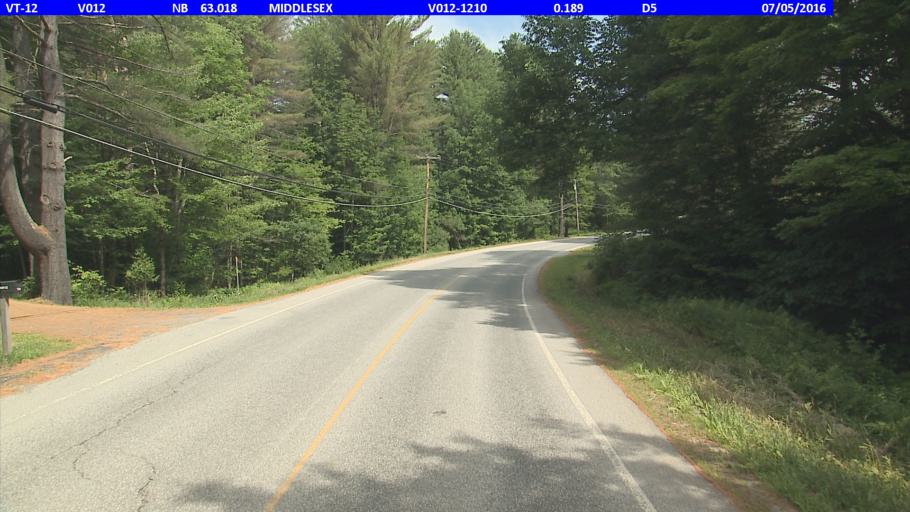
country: US
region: Vermont
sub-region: Washington County
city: Montpelier
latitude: 44.3079
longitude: -72.5804
